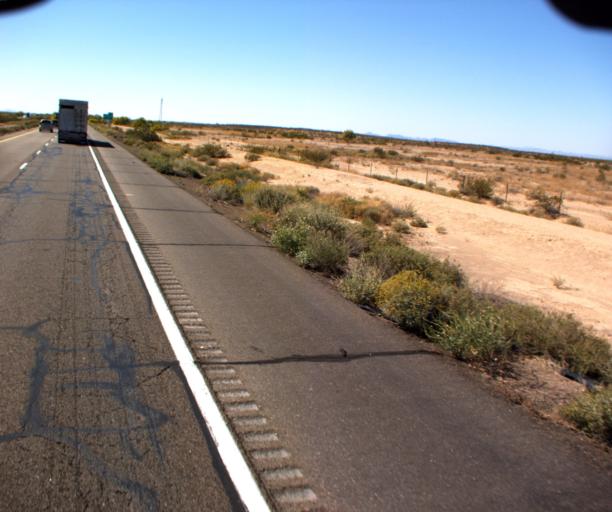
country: US
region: Arizona
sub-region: Maricopa County
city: Gila Bend
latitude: 32.8610
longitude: -113.1883
